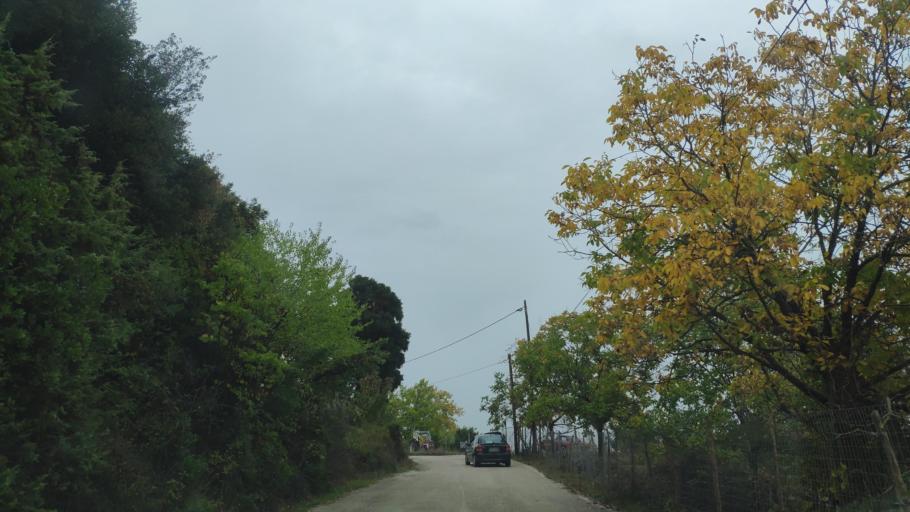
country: GR
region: Epirus
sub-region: Nomos Thesprotias
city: Paramythia
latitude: 39.4701
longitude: 20.6700
